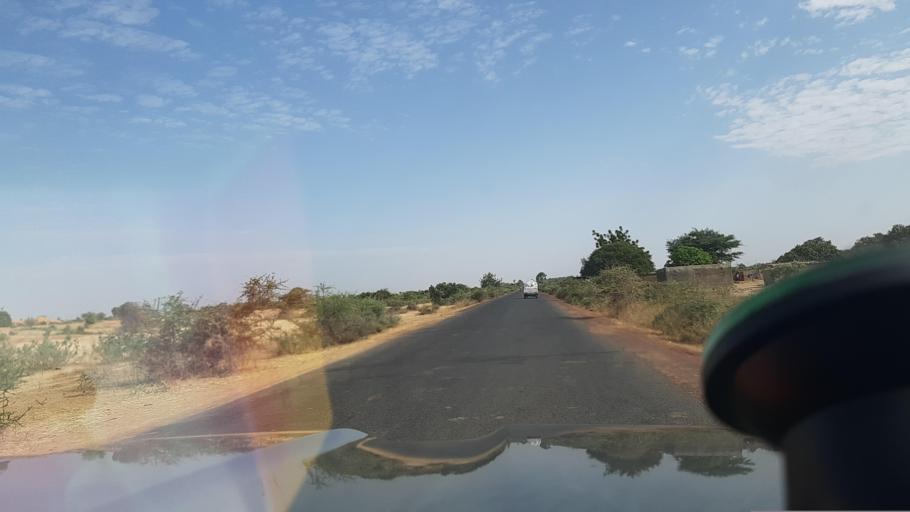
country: ML
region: Segou
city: Markala
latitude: 13.6980
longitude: -6.0966
